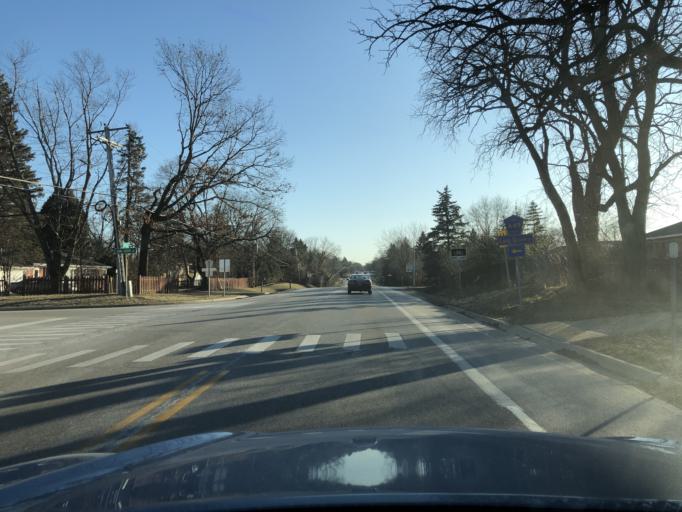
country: US
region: Illinois
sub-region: Lake County
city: Deer Park
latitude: 42.1617
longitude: -88.1018
